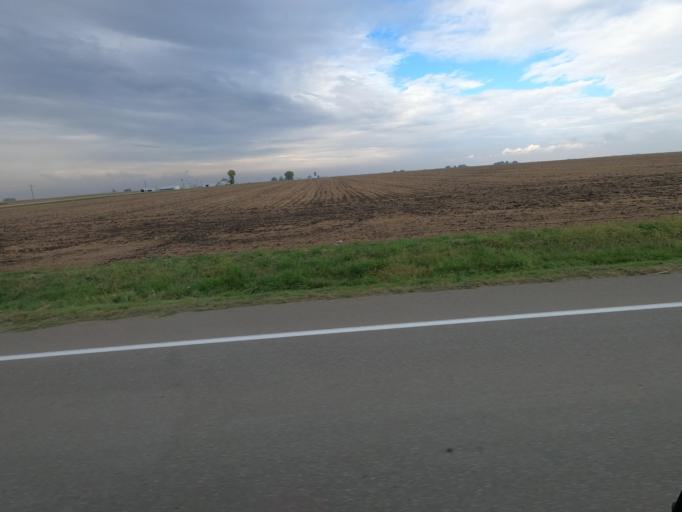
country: US
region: Iowa
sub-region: Henry County
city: Mount Pleasant
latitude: 40.7848
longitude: -91.6207
